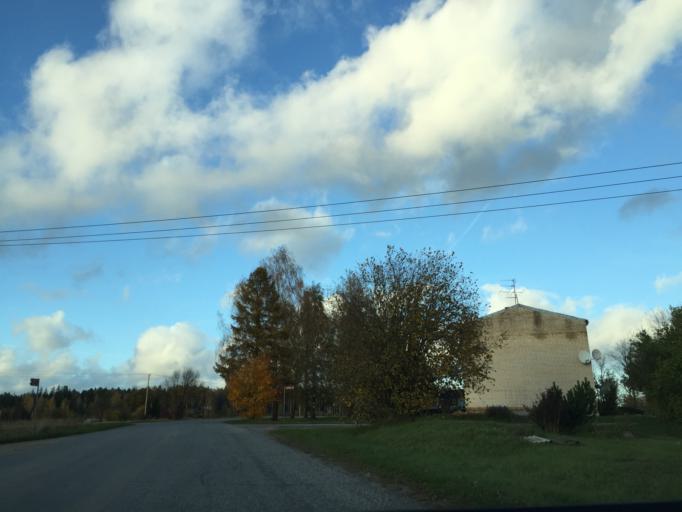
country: LV
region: Ogre
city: Jumprava
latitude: 56.7804
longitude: 25.0099
